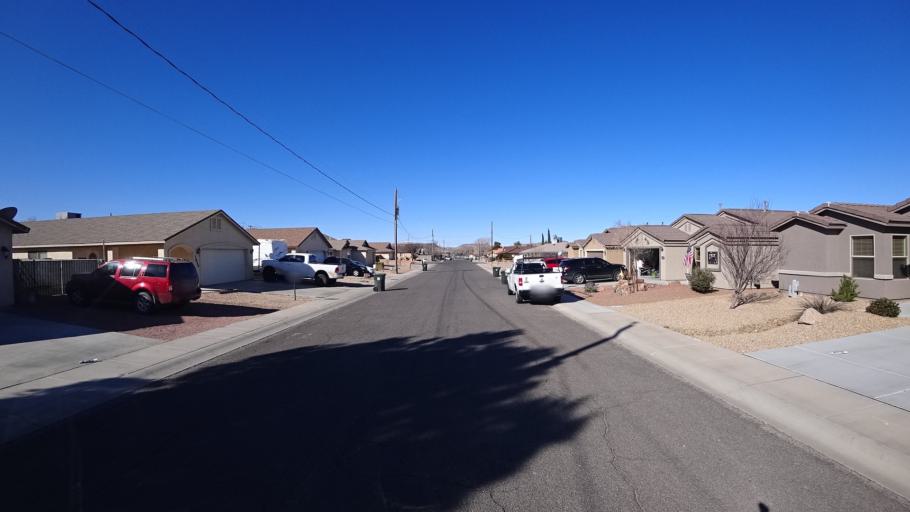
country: US
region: Arizona
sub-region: Mohave County
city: Kingman
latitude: 35.2007
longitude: -114.0126
